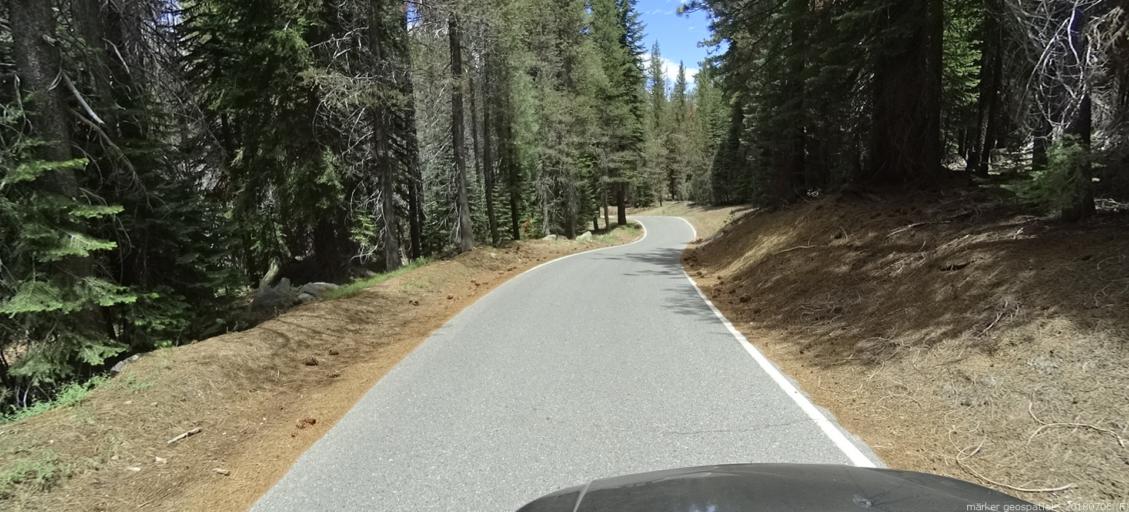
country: US
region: California
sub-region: Madera County
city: Oakhurst
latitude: 37.4459
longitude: -119.4499
